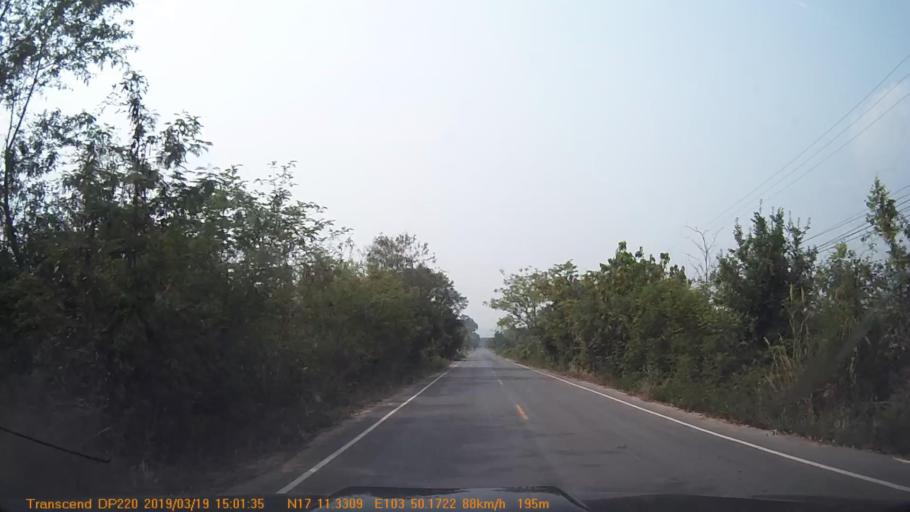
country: TH
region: Sakon Nakhon
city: Kut Bak
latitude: 17.1892
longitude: 103.8360
